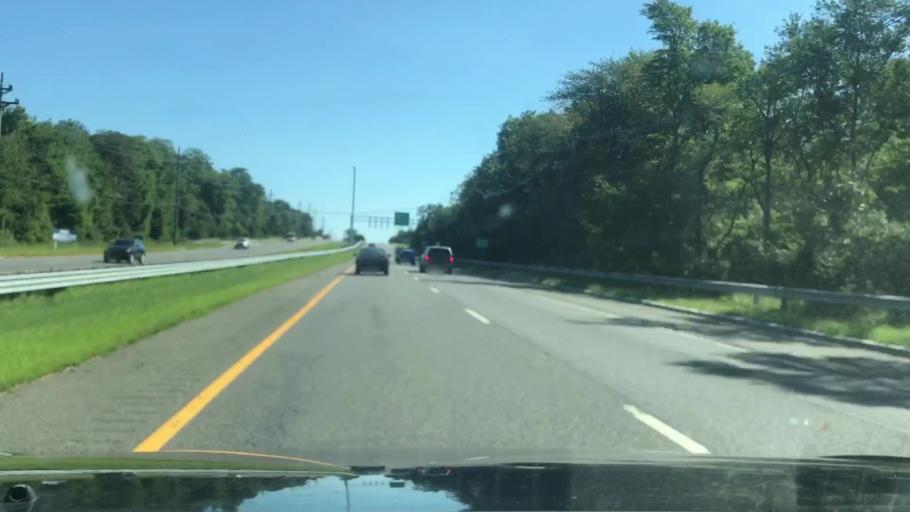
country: US
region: New Jersey
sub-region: Monmouth County
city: Shark River Hills
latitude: 40.1709
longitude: -74.0779
